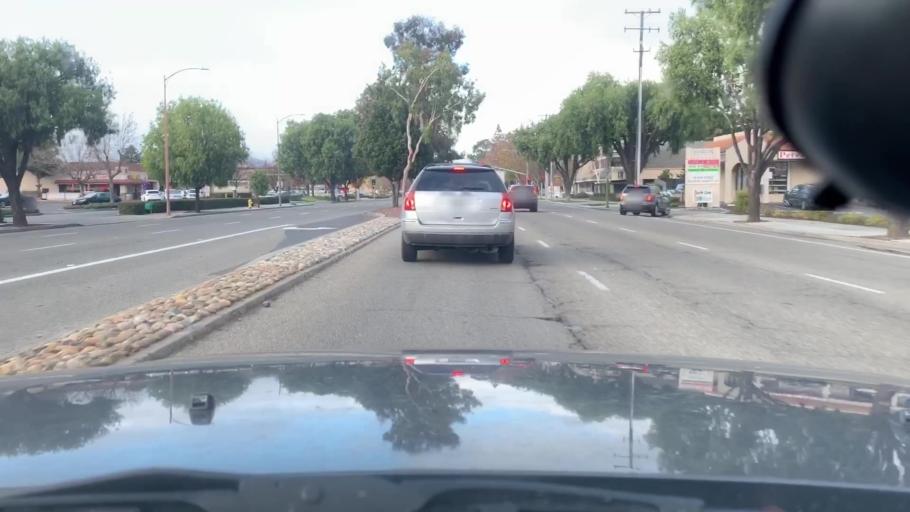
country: US
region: California
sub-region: Santa Clara County
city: Campbell
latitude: 37.2943
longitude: -121.9636
